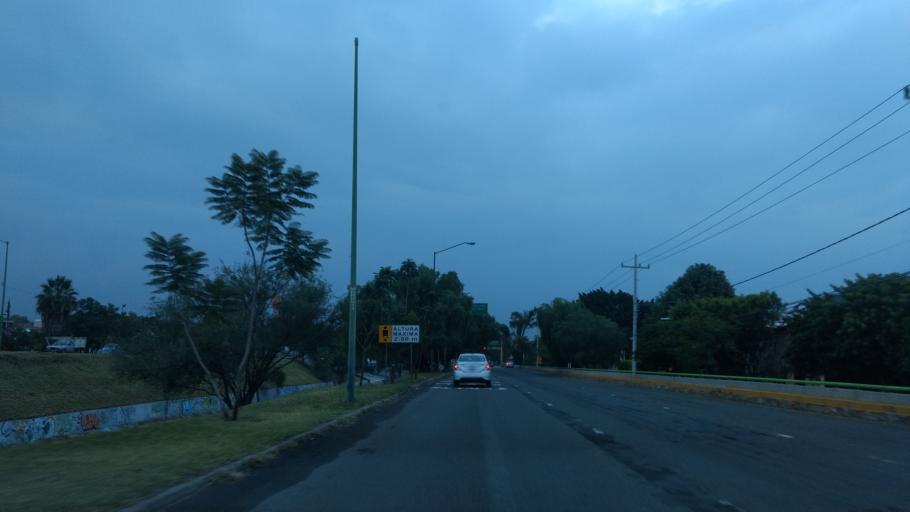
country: MX
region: Guanajuato
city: Leon
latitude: 21.1102
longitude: -101.6637
